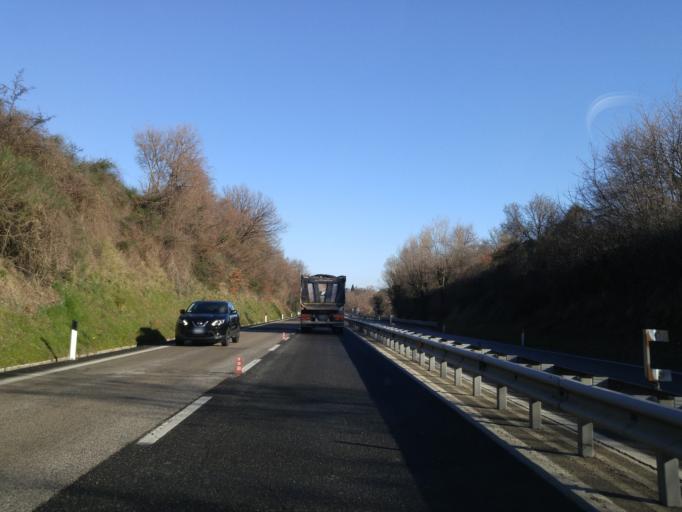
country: IT
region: The Marches
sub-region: Provincia di Pesaro e Urbino
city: Sant'Ippolito
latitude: 43.6931
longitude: 12.8595
